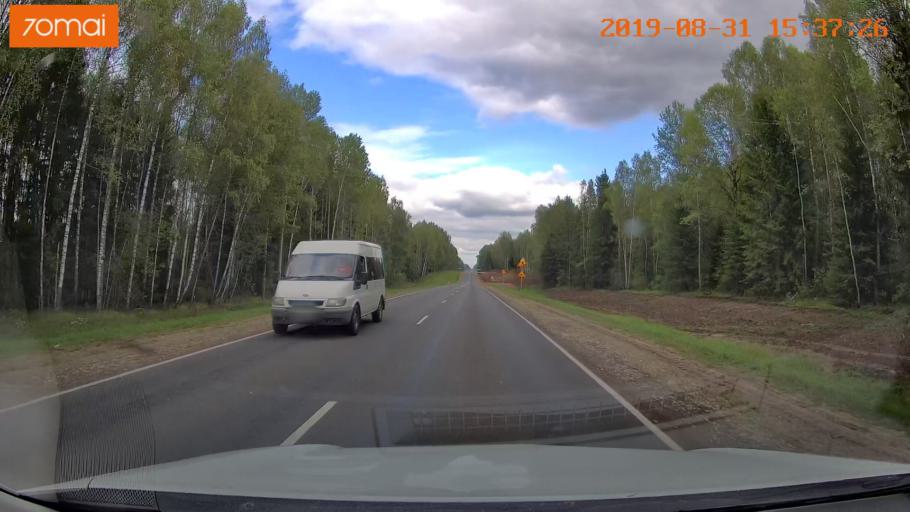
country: RU
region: Kaluga
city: Mosal'sk
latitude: 54.6182
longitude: 34.7842
